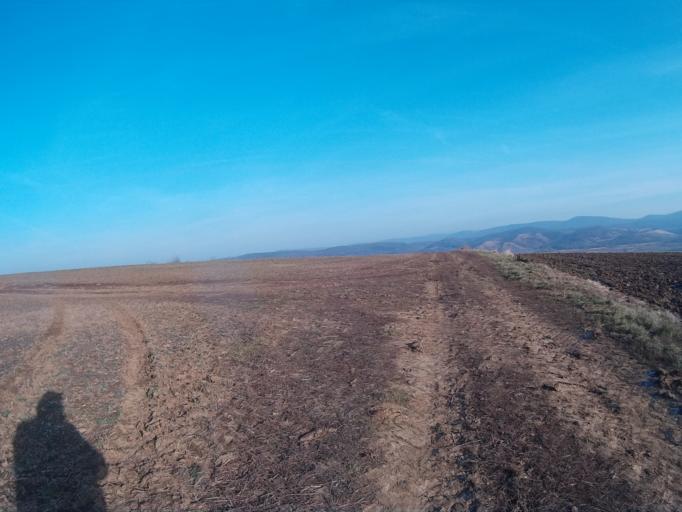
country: HU
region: Nograd
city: Bercel
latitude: 47.9331
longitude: 19.4304
